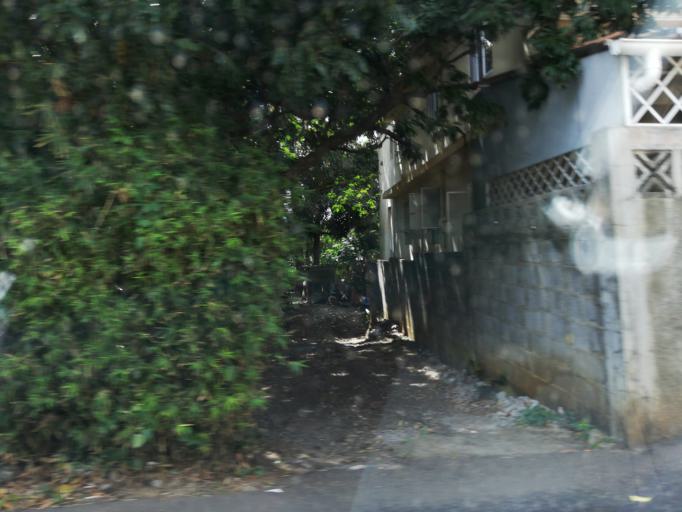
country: MU
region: Moka
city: Moka
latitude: -20.2191
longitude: 57.4702
